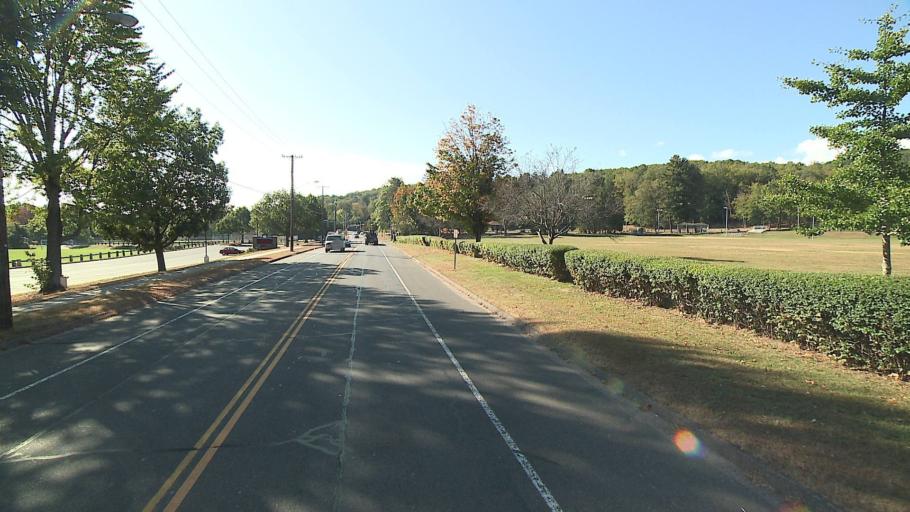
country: US
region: Connecticut
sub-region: Hartford County
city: Bristol
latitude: 41.6870
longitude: -72.9252
